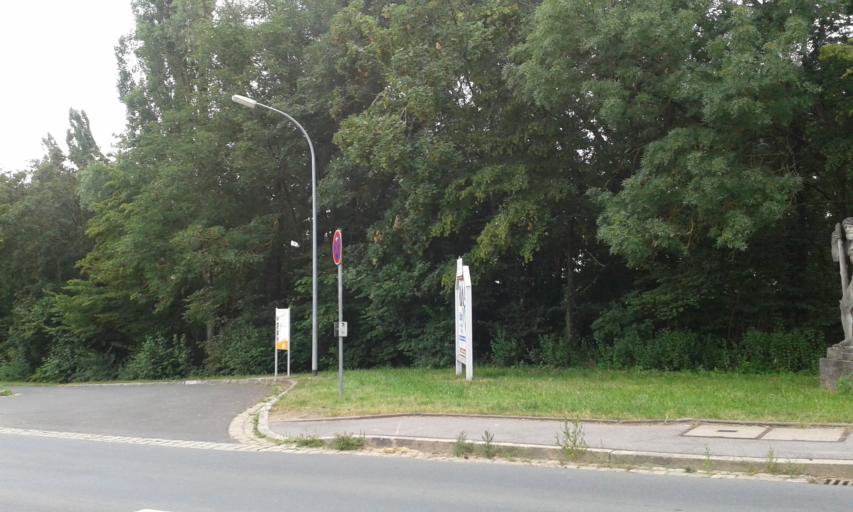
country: DE
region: Bavaria
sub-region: Regierungsbezirk Unterfranken
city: Hassfurt
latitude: 50.0291
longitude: 10.5068
